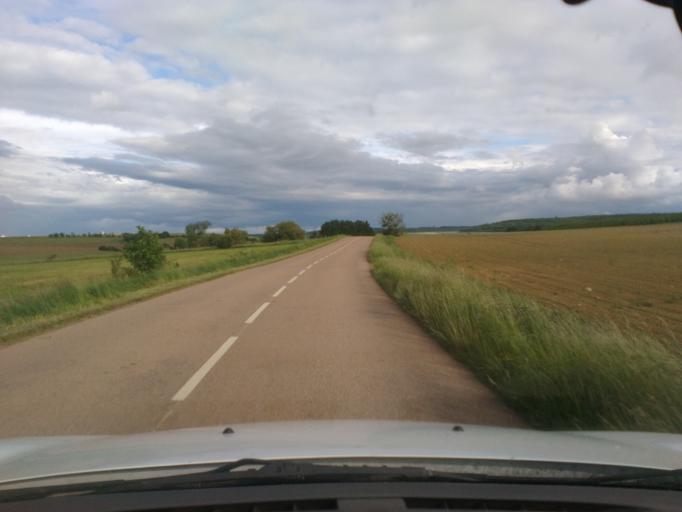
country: FR
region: Lorraine
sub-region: Departement des Vosges
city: Mirecourt
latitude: 48.3247
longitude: 6.0429
